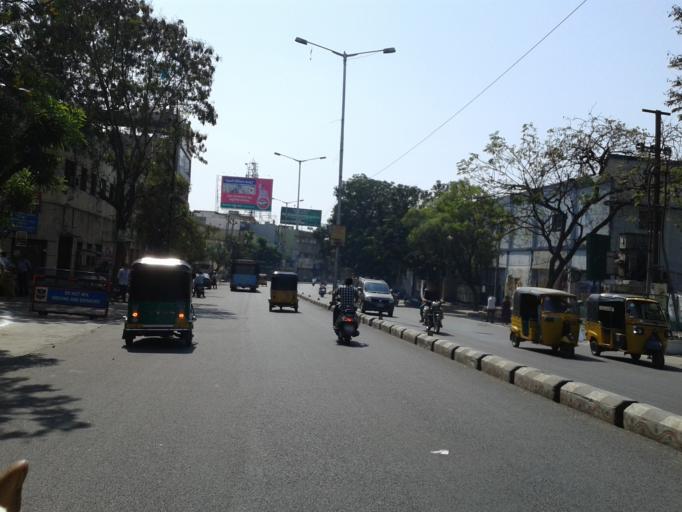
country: IN
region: Telangana
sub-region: Hyderabad
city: Malkajgiri
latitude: 17.4395
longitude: 78.4952
